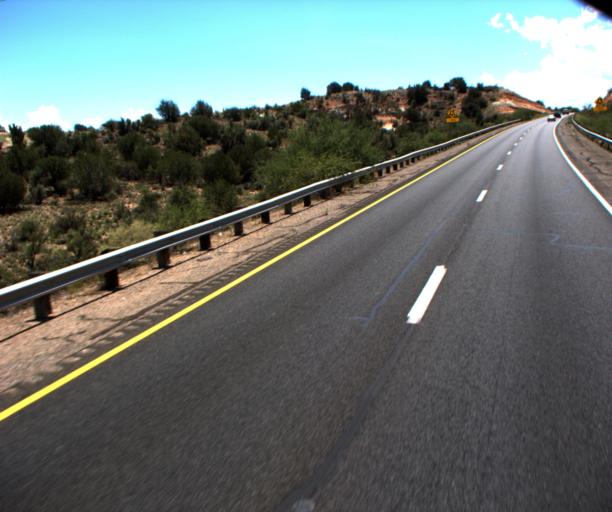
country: US
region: Arizona
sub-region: Yavapai County
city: Verde Village
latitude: 34.6768
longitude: -111.9726
